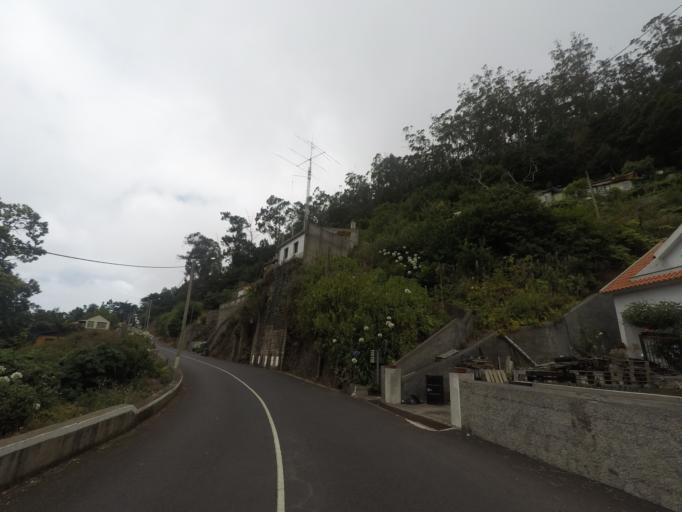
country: PT
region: Madeira
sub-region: Funchal
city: Nossa Senhora do Monte
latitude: 32.6665
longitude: -16.8720
